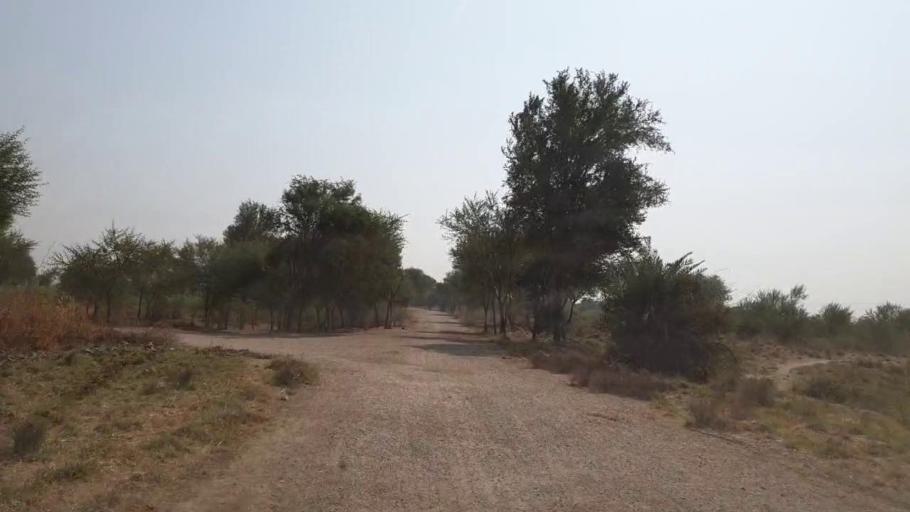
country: PK
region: Sindh
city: Mirpur Khas
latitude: 25.6295
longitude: 69.1454
